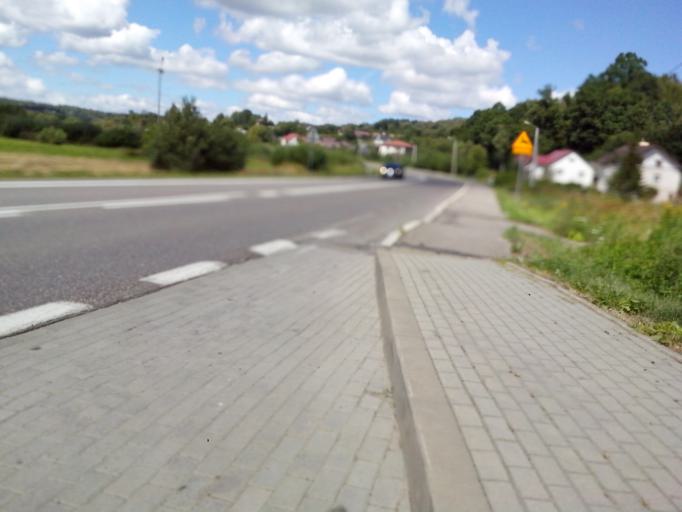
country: PL
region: Subcarpathian Voivodeship
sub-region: Powiat brzozowski
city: Blizne
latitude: 49.7626
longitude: 21.9646
